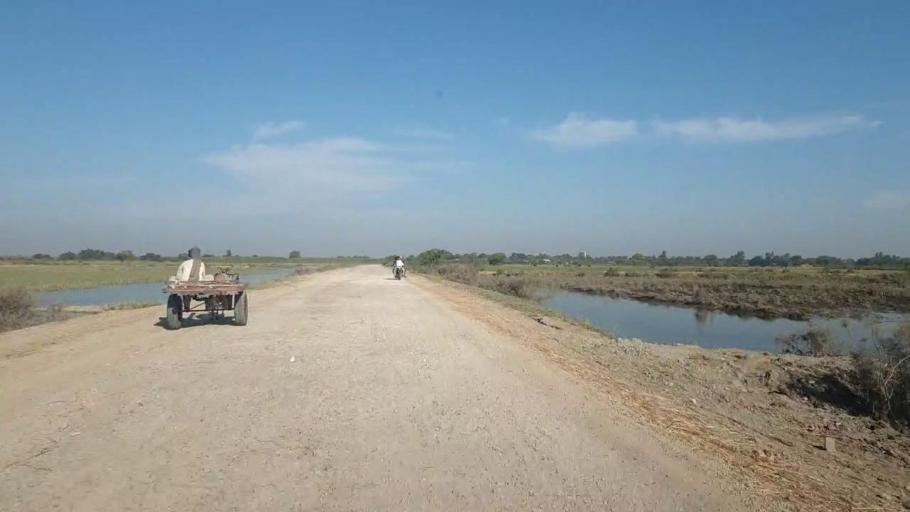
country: PK
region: Sindh
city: Talhar
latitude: 24.9200
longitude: 68.8010
